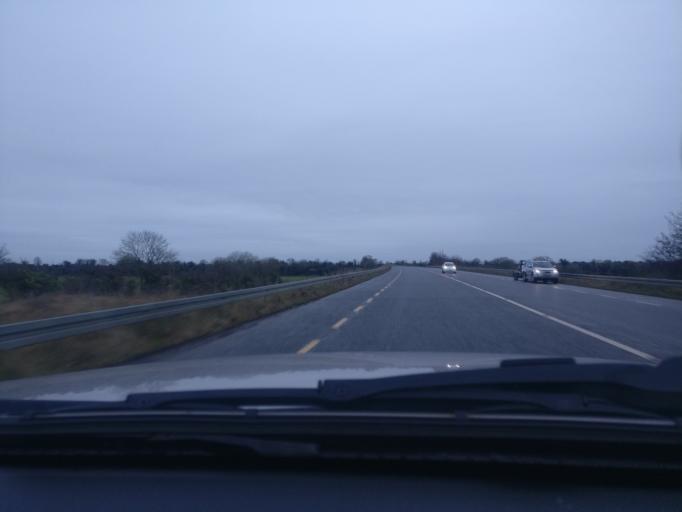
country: IE
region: Leinster
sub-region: An Mhi
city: Dunshaughlin
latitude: 53.5046
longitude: -6.5707
